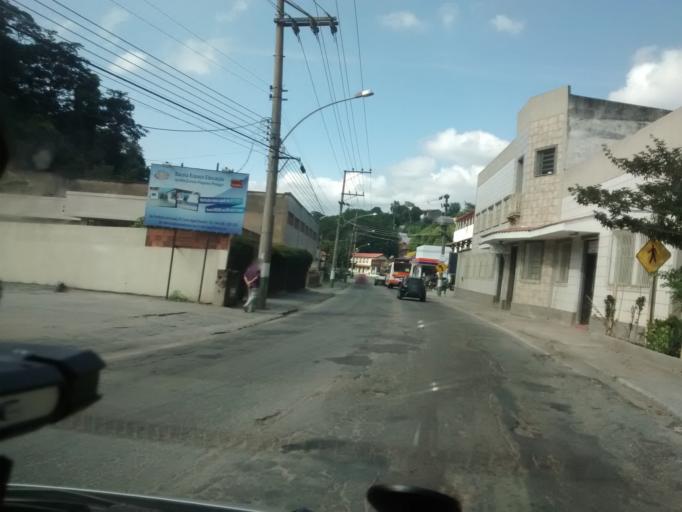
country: BR
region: Rio de Janeiro
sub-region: Miguel Pereira
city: Miguel Pereira
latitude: -22.4585
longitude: -43.4738
